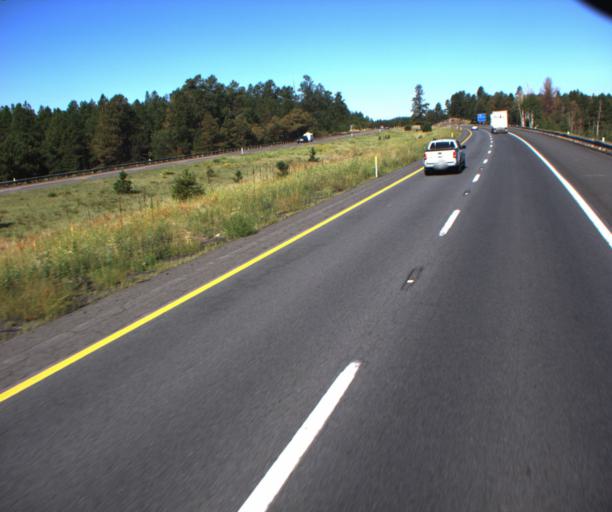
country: US
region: Arizona
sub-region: Coconino County
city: Parks
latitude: 35.2570
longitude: -111.9256
